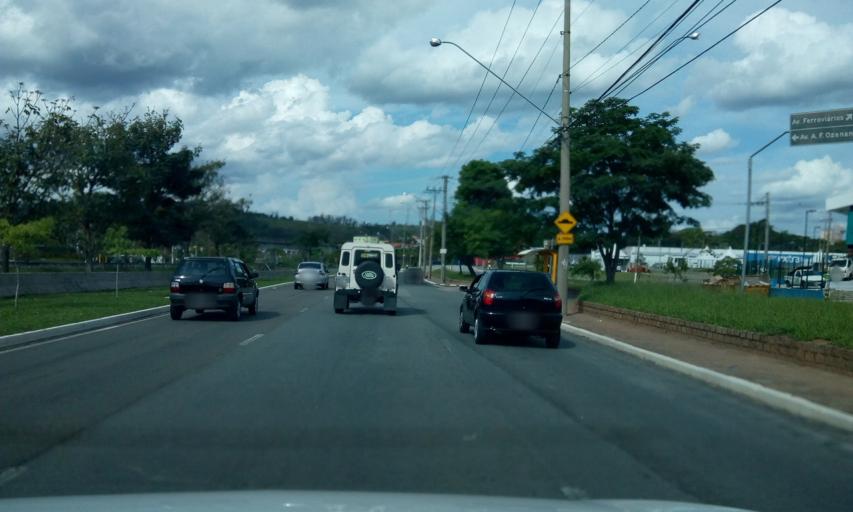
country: BR
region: Sao Paulo
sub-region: Jundiai
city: Jundiai
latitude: -23.1754
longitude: -46.8975
